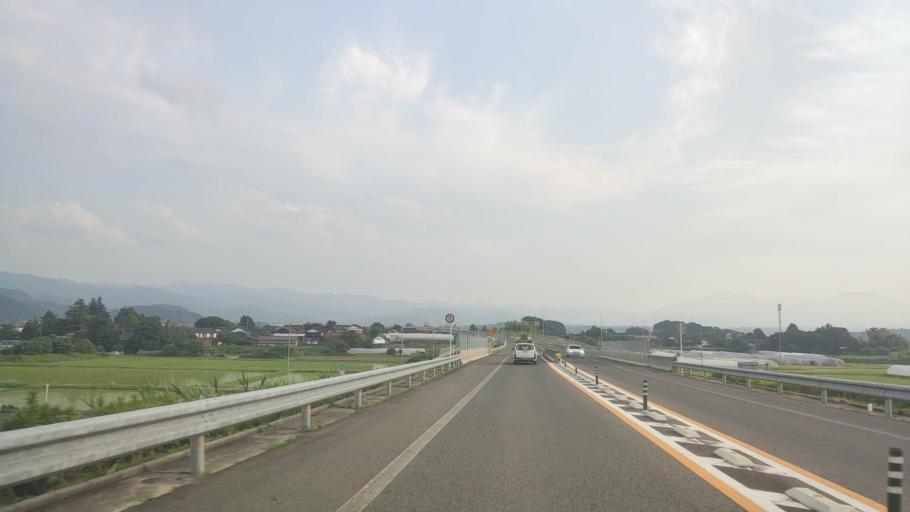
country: JP
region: Tottori
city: Kurayoshi
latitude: 35.4476
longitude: 133.8085
